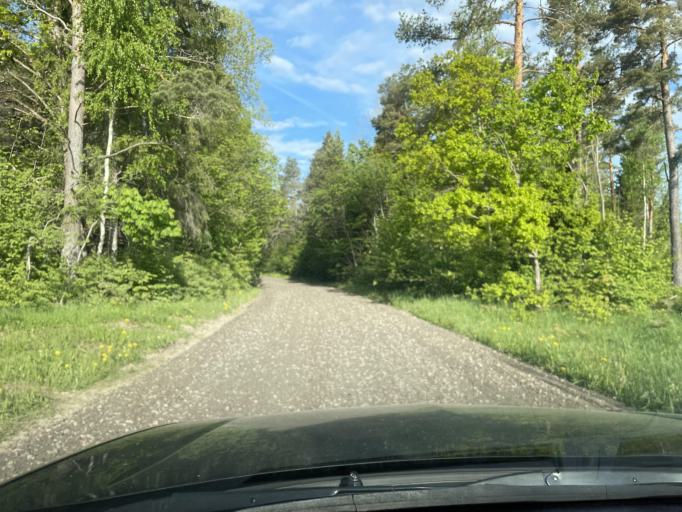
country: EE
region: Harju
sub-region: Keila linn
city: Keila
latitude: 59.3083
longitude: 24.2899
